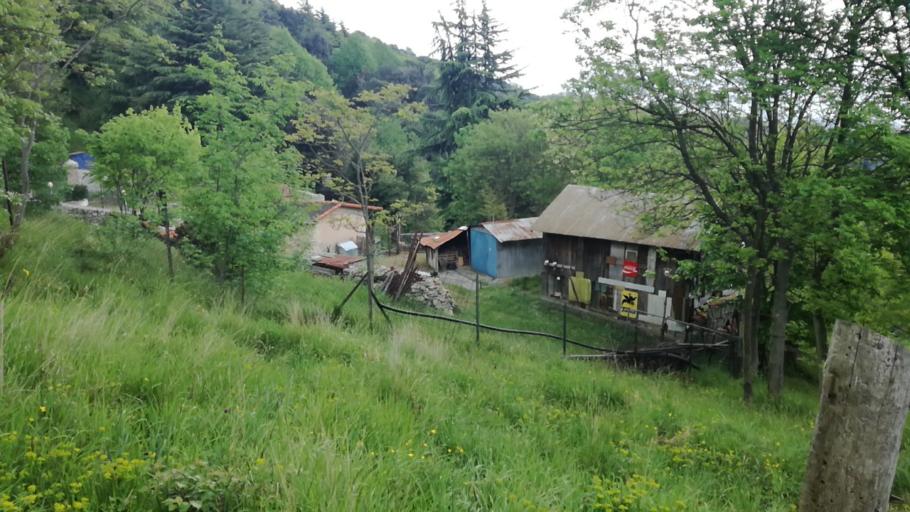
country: IT
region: Liguria
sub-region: Provincia di Genova
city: Genoa
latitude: 44.4383
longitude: 8.9247
